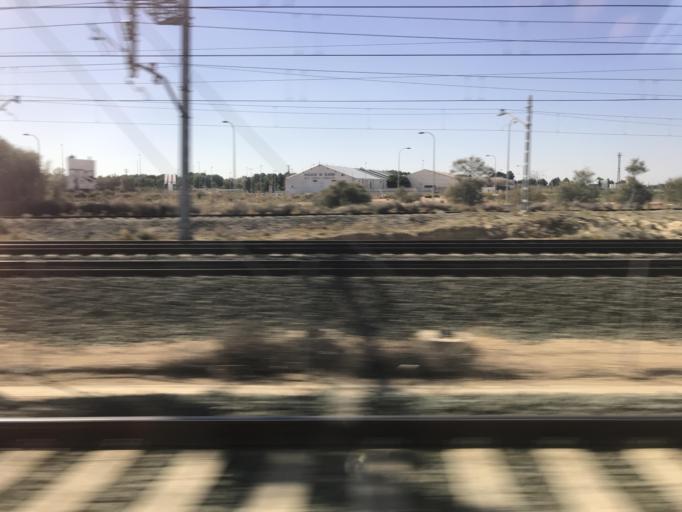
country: ES
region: Castille-La Mancha
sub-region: Provincia de Albacete
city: Albacete
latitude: 39.0138
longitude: -1.8611
